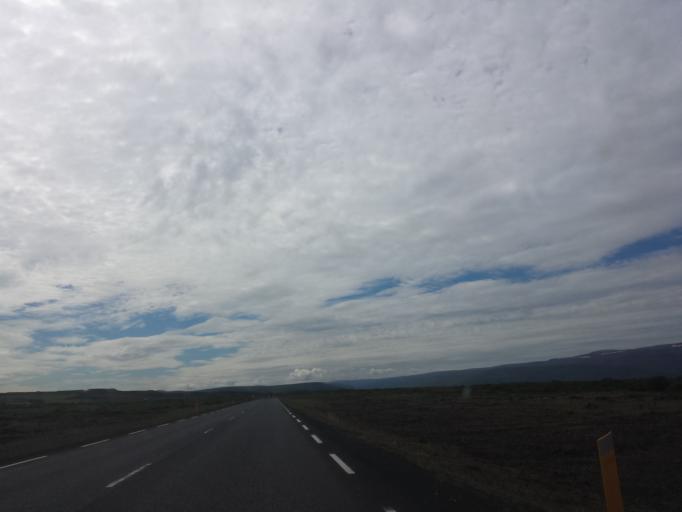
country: IS
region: Northeast
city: Husavik
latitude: 65.9583
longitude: -17.4268
